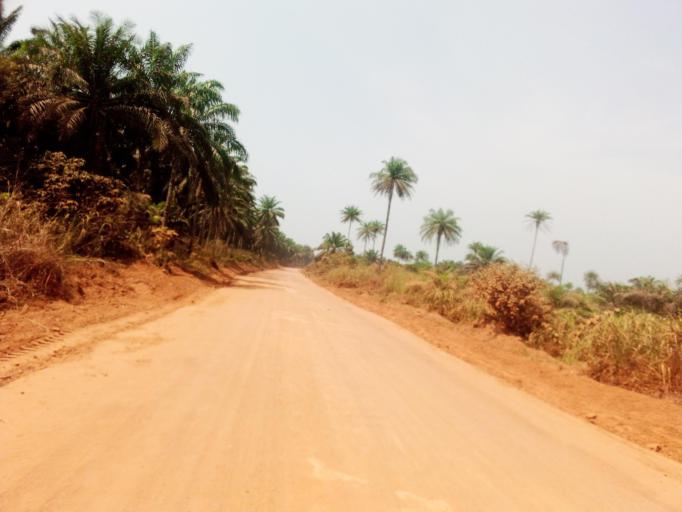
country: SL
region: Southern Province
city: Sumbuya
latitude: 7.6198
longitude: -12.1183
